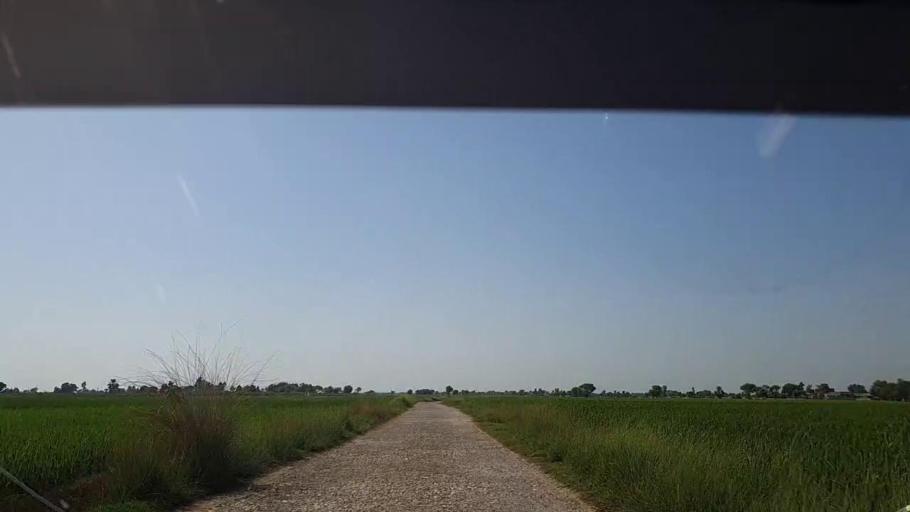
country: PK
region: Sindh
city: Ghauspur
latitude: 28.1791
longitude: 69.0338
